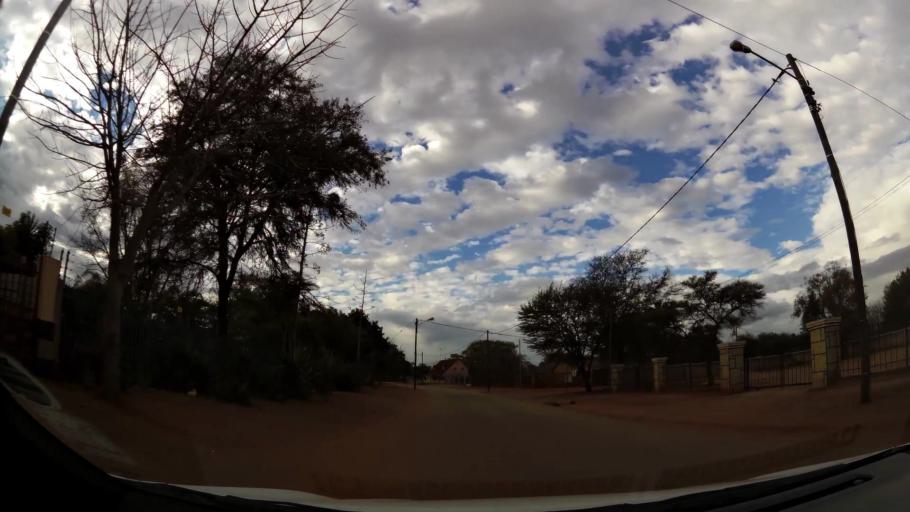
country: ZA
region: Limpopo
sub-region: Waterberg District Municipality
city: Modimolle
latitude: -24.5087
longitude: 28.7231
